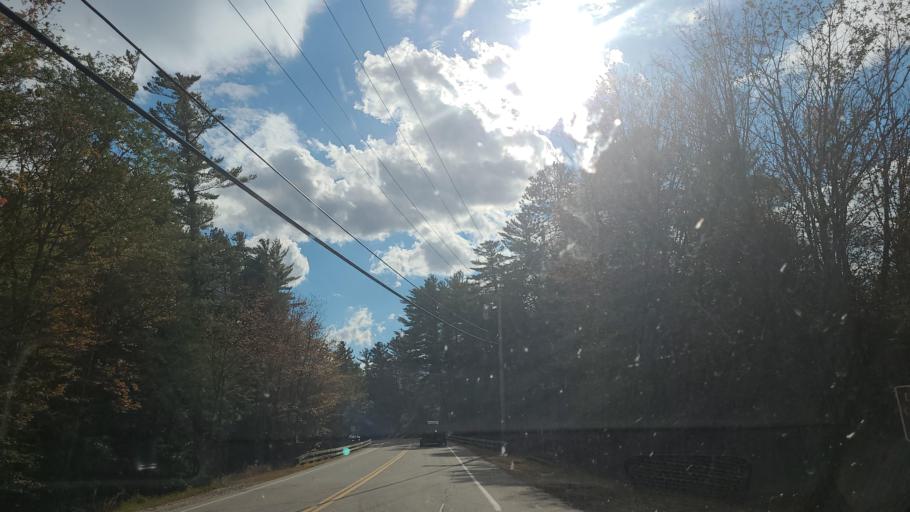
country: US
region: New Hampshire
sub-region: Carroll County
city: North Conway
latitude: 44.0535
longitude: -71.1548
